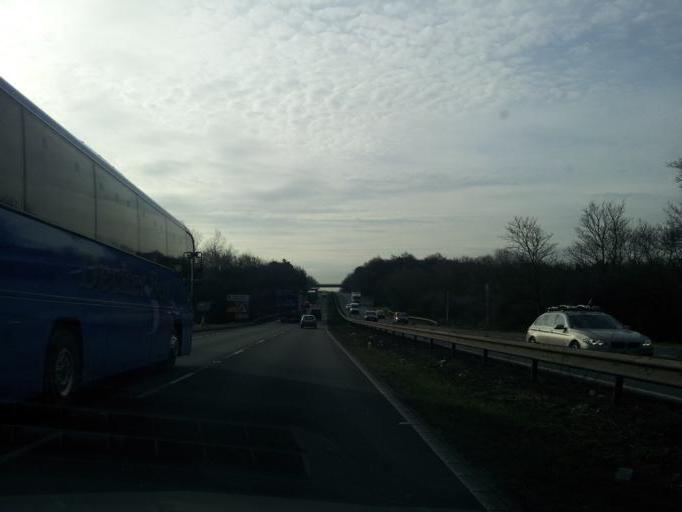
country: GB
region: England
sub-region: Peterborough
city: Thornhaugh
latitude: 52.5894
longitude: -0.4162
